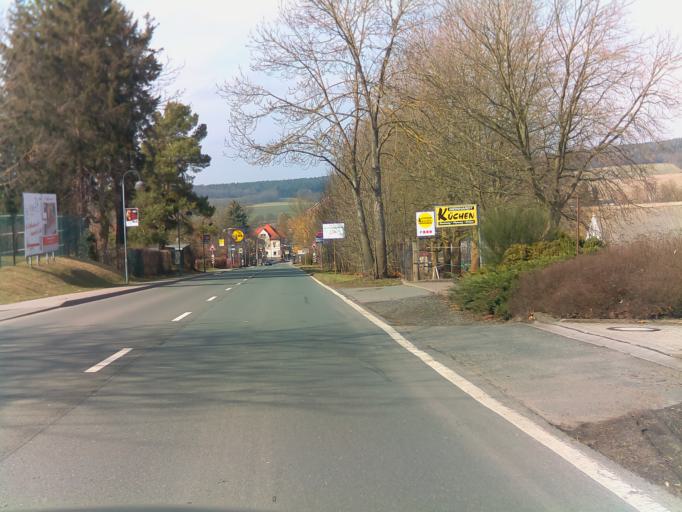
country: DE
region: Thuringia
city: Neustadt (Orla)
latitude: 50.7312
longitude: 11.7556
